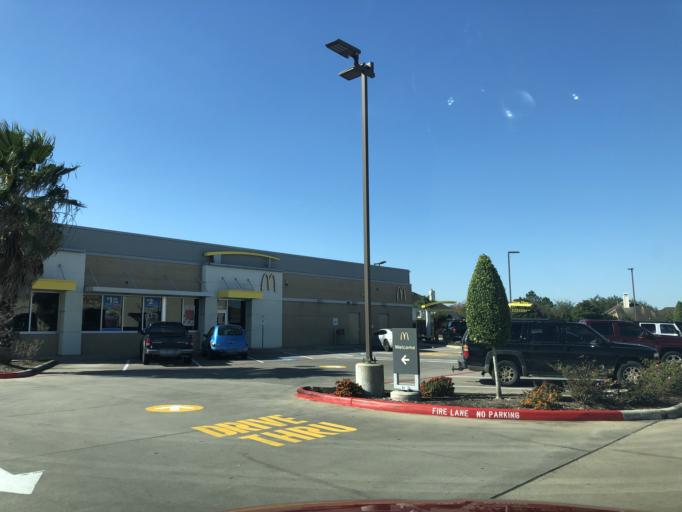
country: US
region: Texas
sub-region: Galveston County
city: Dickinson
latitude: 29.5043
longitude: -95.0434
